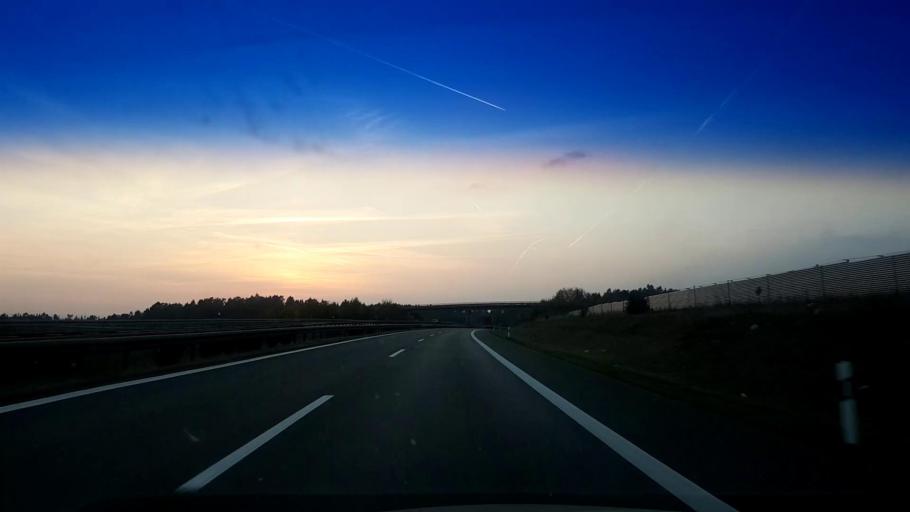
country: DE
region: Bavaria
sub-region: Upper Franconia
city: Wonsees
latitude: 50.0060
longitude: 11.2621
